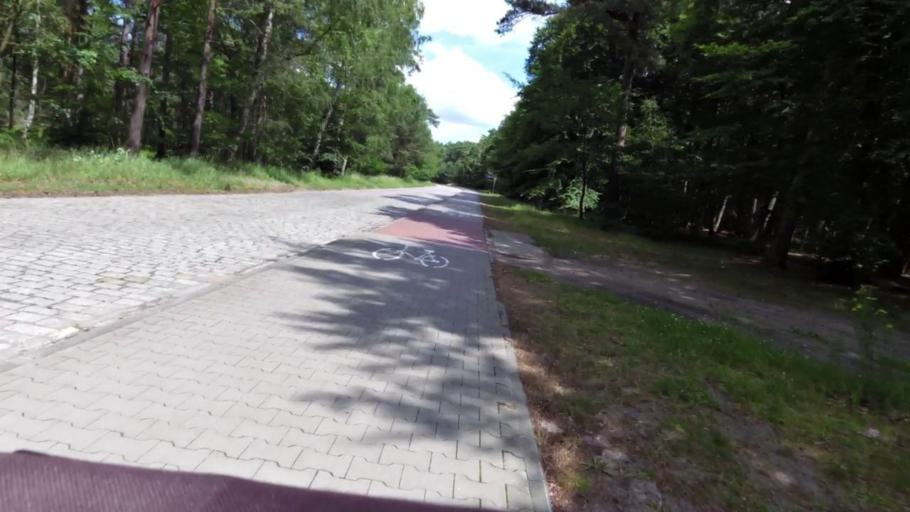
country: PL
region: West Pomeranian Voivodeship
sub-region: Powiat gryficki
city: Mrzezyno
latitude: 54.1359
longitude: 15.2725
